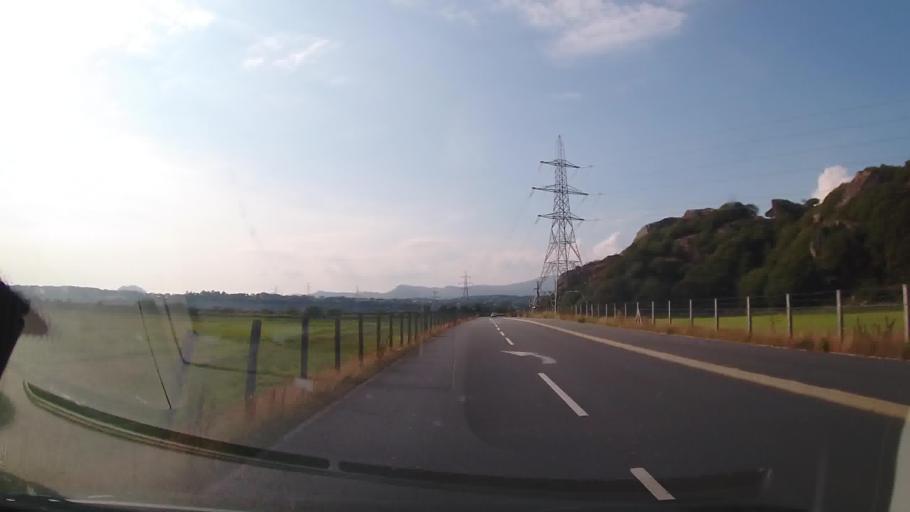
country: GB
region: Wales
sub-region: Gwynedd
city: Penrhyndeudraeth
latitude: 52.9194
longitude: -4.0539
